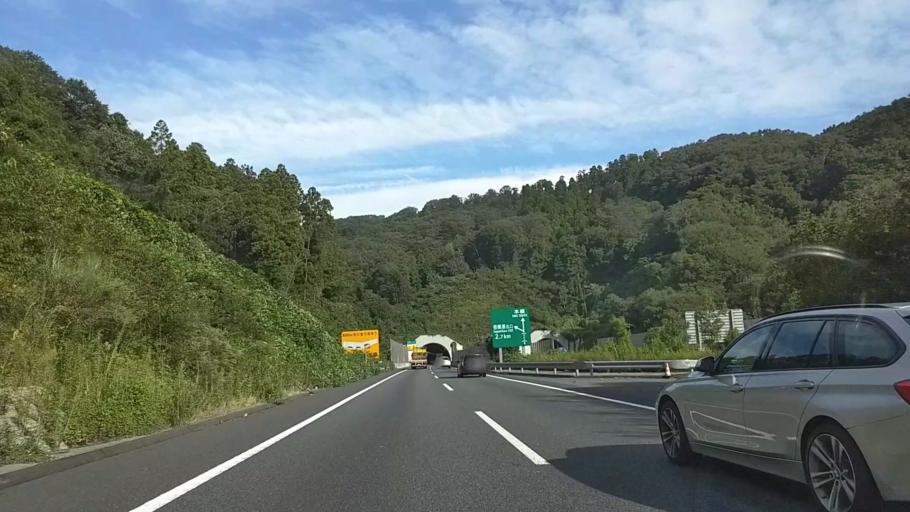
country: JP
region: Tokyo
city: Hachioji
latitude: 35.5581
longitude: 139.3133
